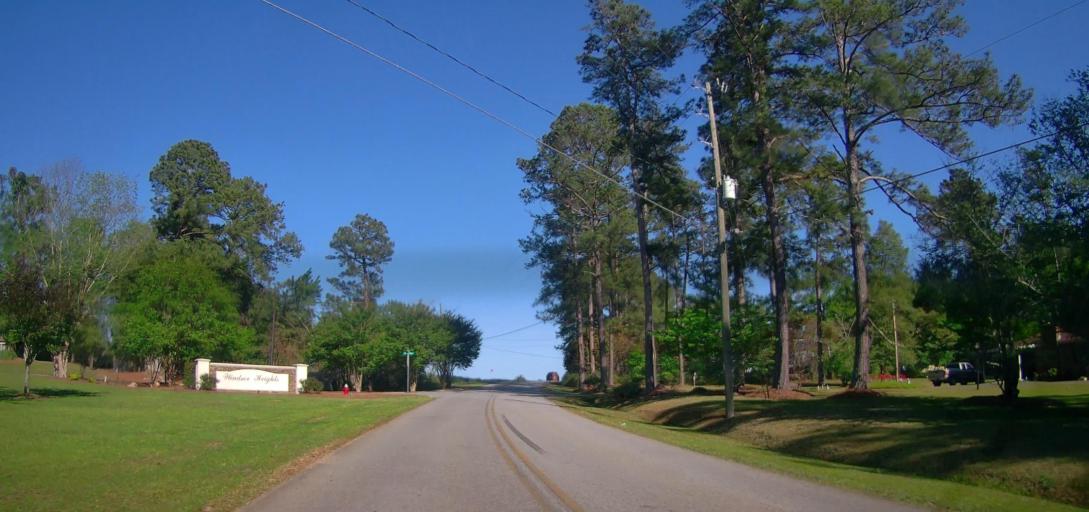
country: US
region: Georgia
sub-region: Houston County
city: Robins Air Force Base
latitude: 32.5356
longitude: -83.5916
